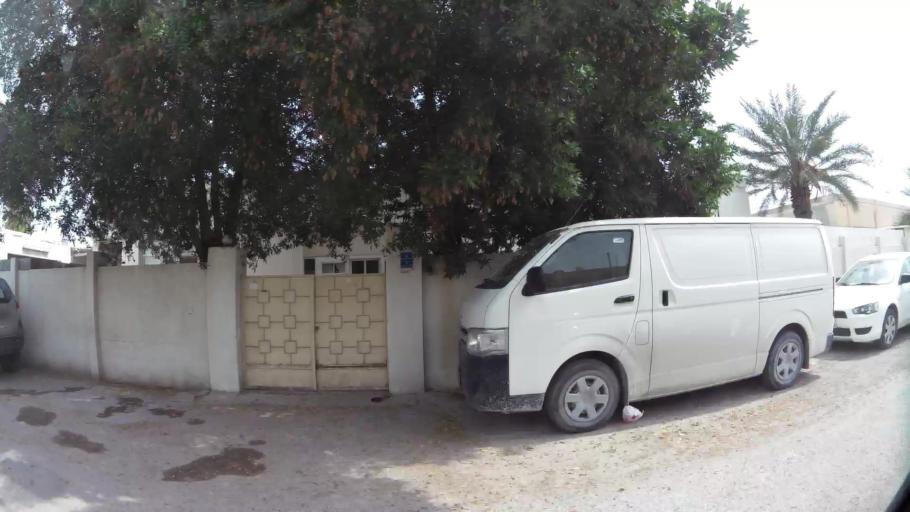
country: QA
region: Baladiyat ad Dawhah
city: Doha
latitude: 25.2648
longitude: 51.4934
